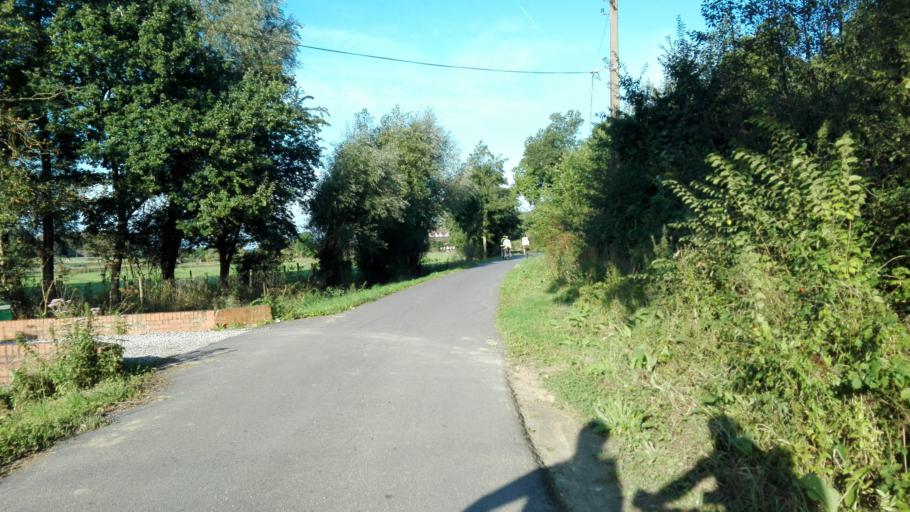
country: FR
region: Nord-Pas-de-Calais
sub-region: Departement du Pas-de-Calais
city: Eperlecques
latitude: 50.8251
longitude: 2.1725
